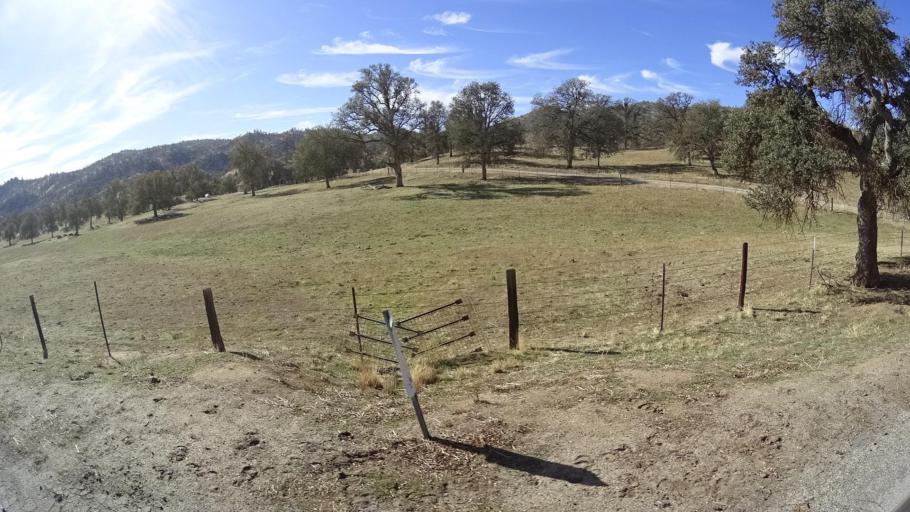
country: US
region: California
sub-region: Kern County
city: Alta Sierra
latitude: 35.6230
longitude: -118.7456
